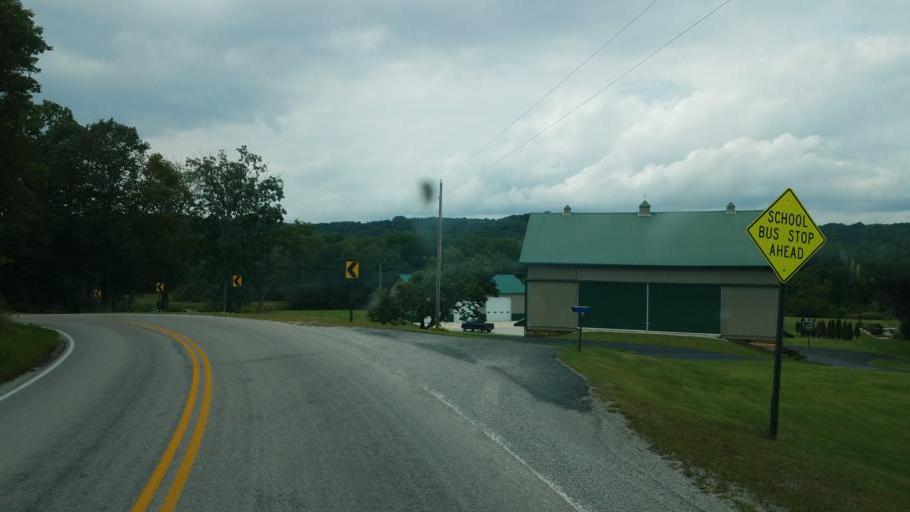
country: US
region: Ohio
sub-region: Sandusky County
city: Bellville
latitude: 40.6334
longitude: -82.3743
